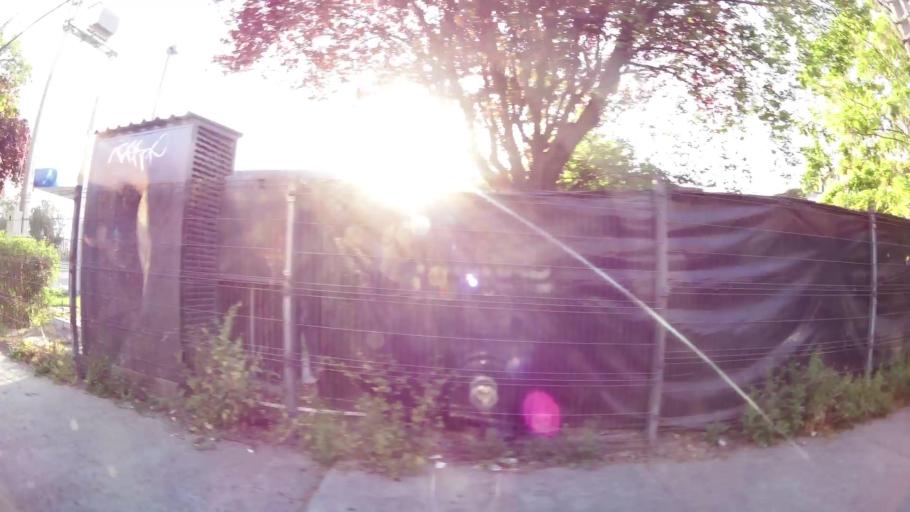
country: CL
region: Santiago Metropolitan
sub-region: Provincia de Santiago
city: Villa Presidente Frei, Nunoa, Santiago, Chile
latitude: -33.5205
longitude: -70.5808
